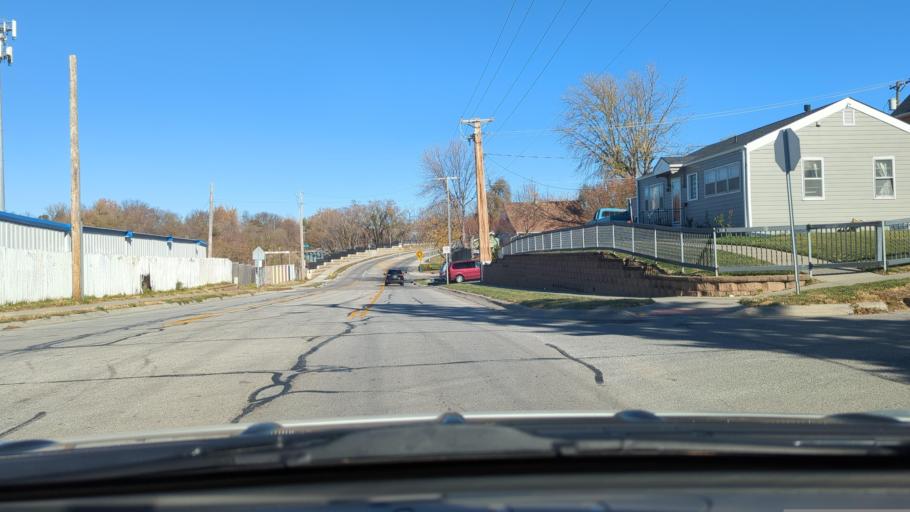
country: US
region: Nebraska
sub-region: Sarpy County
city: La Vista
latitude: 41.2035
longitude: -95.9770
